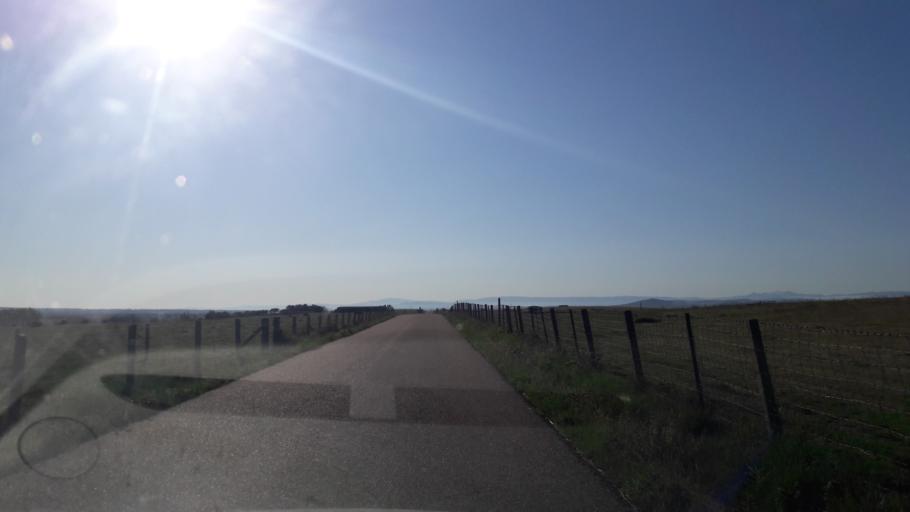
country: ES
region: Castille and Leon
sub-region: Provincia de Salamanca
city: Herguijuela del Campo
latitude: 40.6318
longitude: -5.8750
